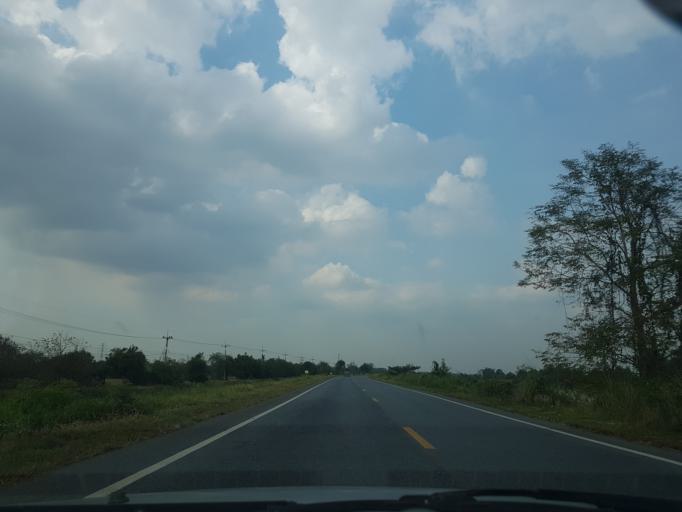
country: TH
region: Phra Nakhon Si Ayutthaya
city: Phachi
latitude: 14.4805
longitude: 100.7415
